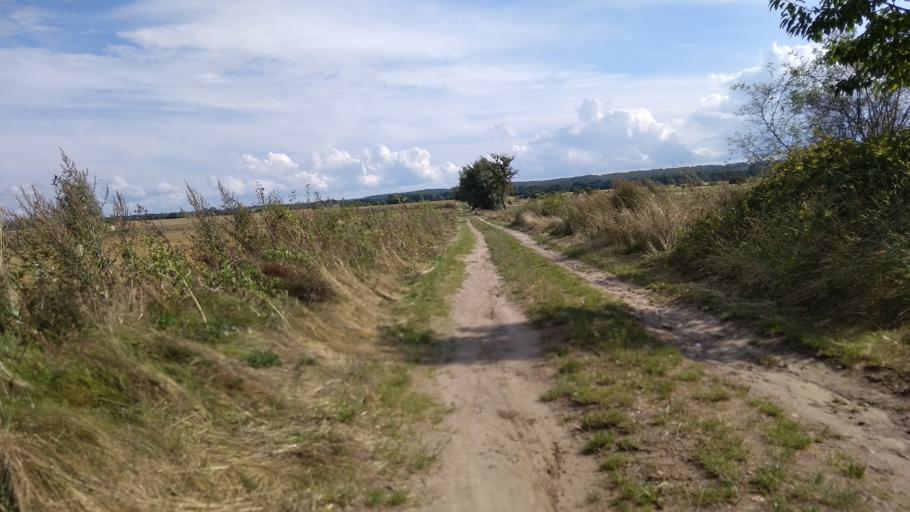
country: PL
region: West Pomeranian Voivodeship
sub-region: Powiat slawienski
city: Darlowo
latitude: 54.5091
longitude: 16.5173
